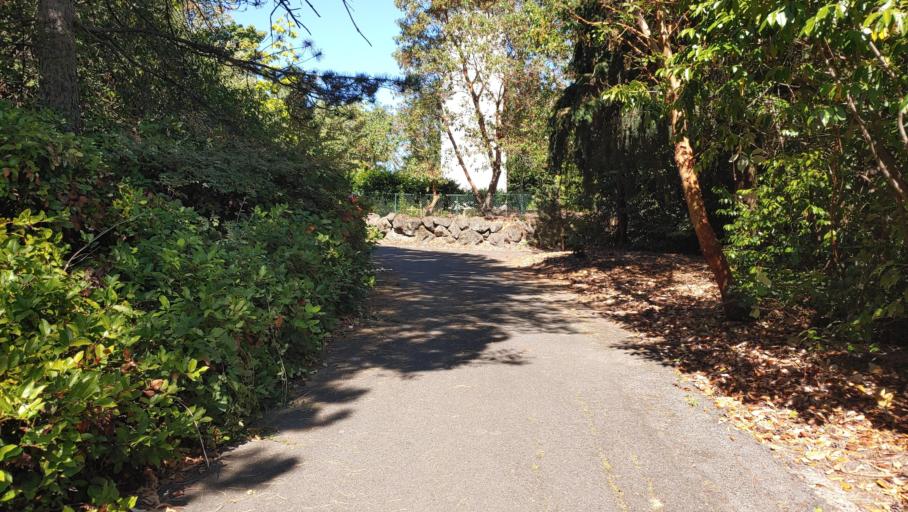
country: US
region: Washington
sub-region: King County
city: Tukwila
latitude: 47.4711
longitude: -122.2426
